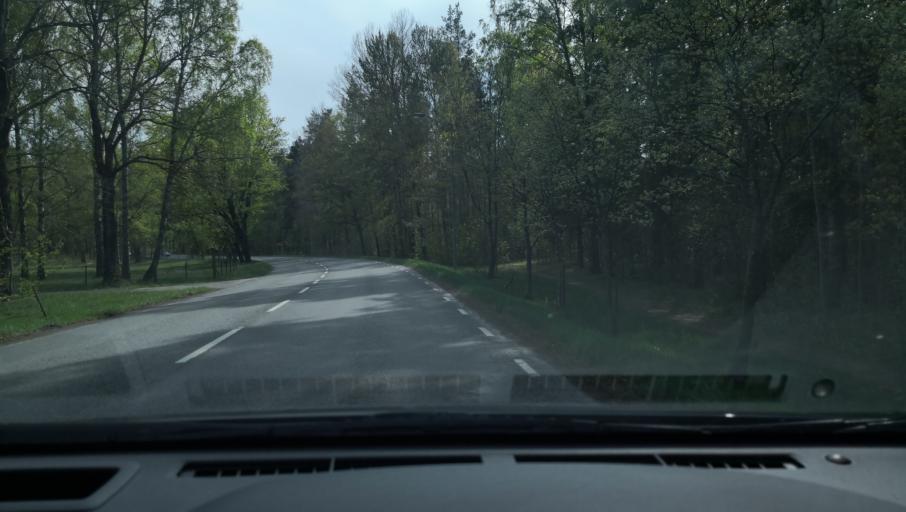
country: SE
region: OErebro
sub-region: Kumla Kommun
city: Kumla
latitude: 59.0934
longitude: 15.1589
